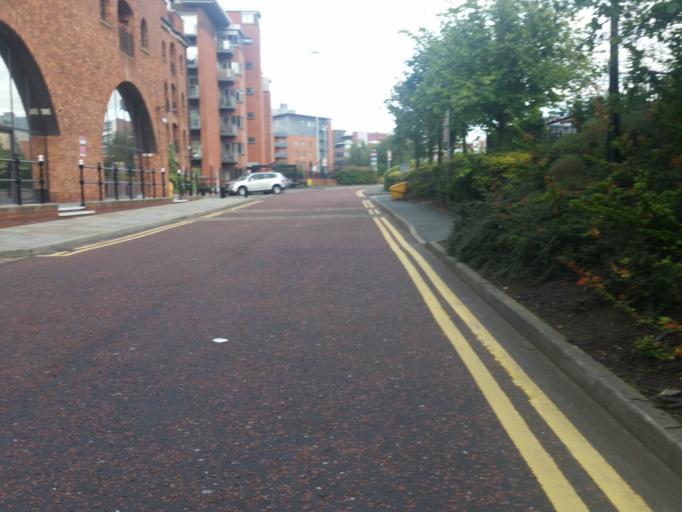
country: GB
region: England
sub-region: Manchester
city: Hulme
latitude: 53.4730
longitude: -2.2563
